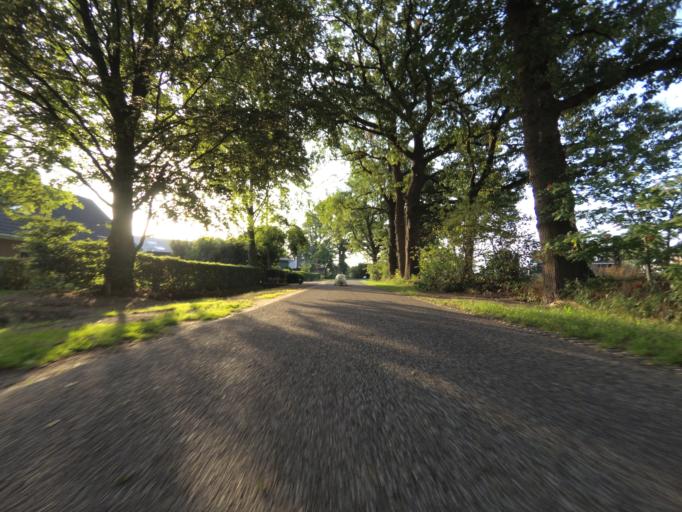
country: NL
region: Gelderland
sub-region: Gemeente Lochem
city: Laren
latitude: 52.2774
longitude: 6.3588
